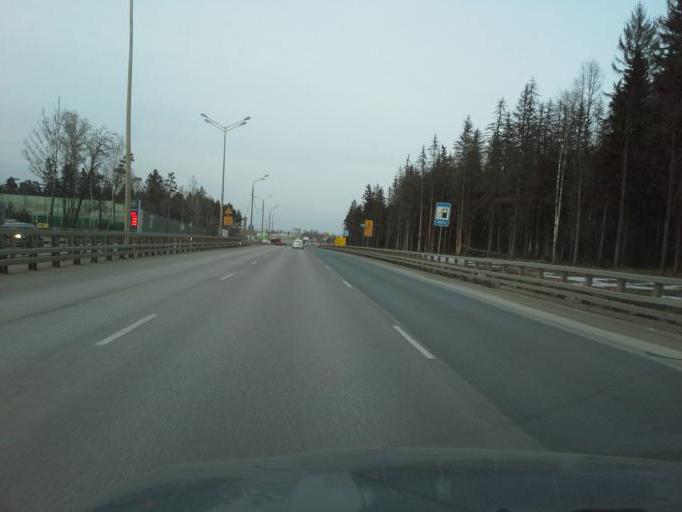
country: RU
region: Moskovskaya
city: Lesnoy Gorodok
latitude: 55.6455
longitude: 37.2442
